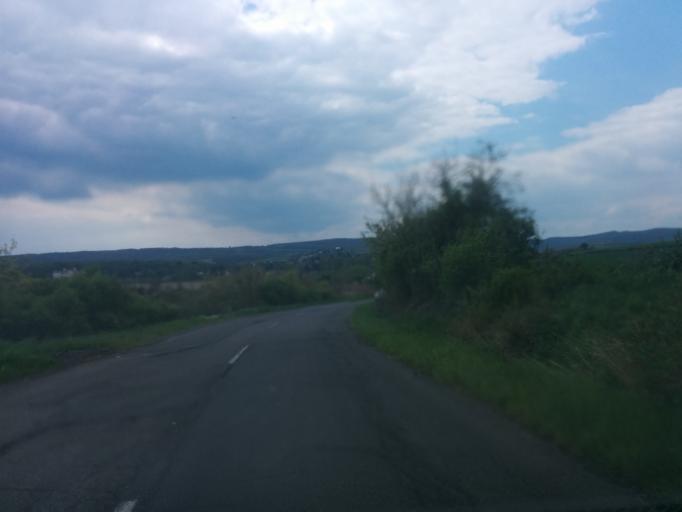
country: HU
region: Nograd
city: Bujak
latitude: 47.8272
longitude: 19.5485
